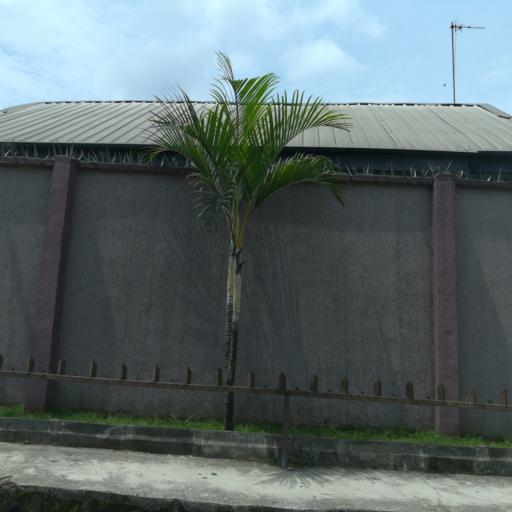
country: NG
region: Rivers
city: Port Harcourt
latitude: 4.7818
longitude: 7.0400
